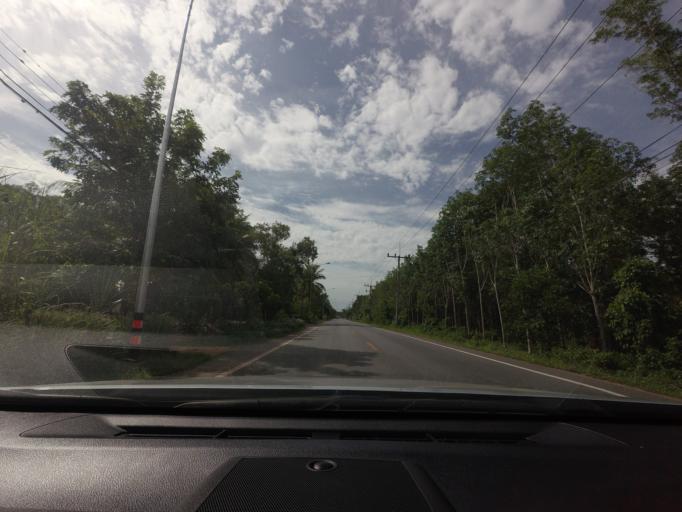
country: TH
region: Songkhla
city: Khlong Hoi Khong
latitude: 6.8959
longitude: 100.4144
